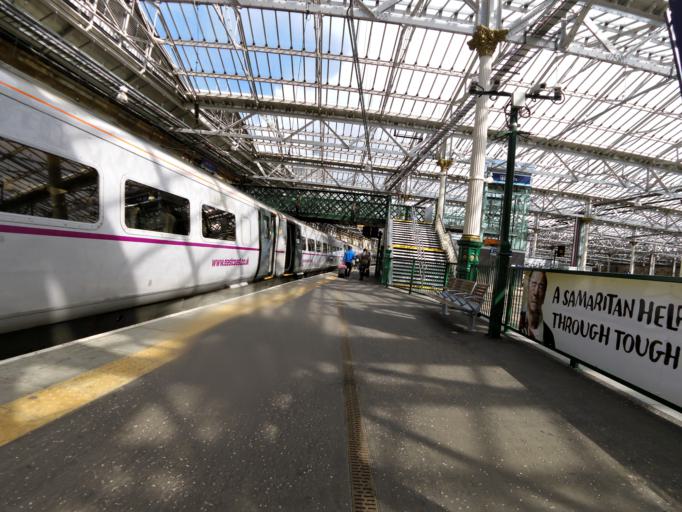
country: GB
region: Scotland
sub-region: Edinburgh
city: Edinburgh
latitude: 55.9528
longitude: -3.1878
